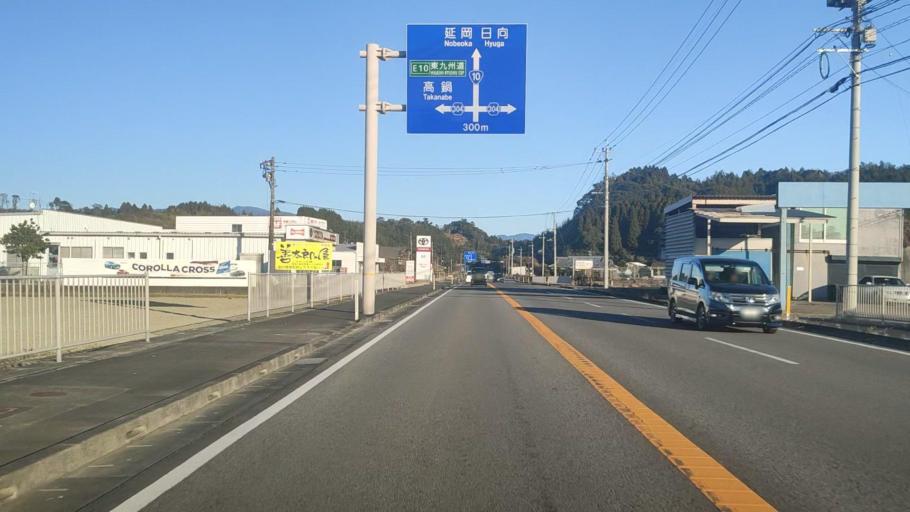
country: JP
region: Miyazaki
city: Takanabe
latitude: 32.1426
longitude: 131.5268
